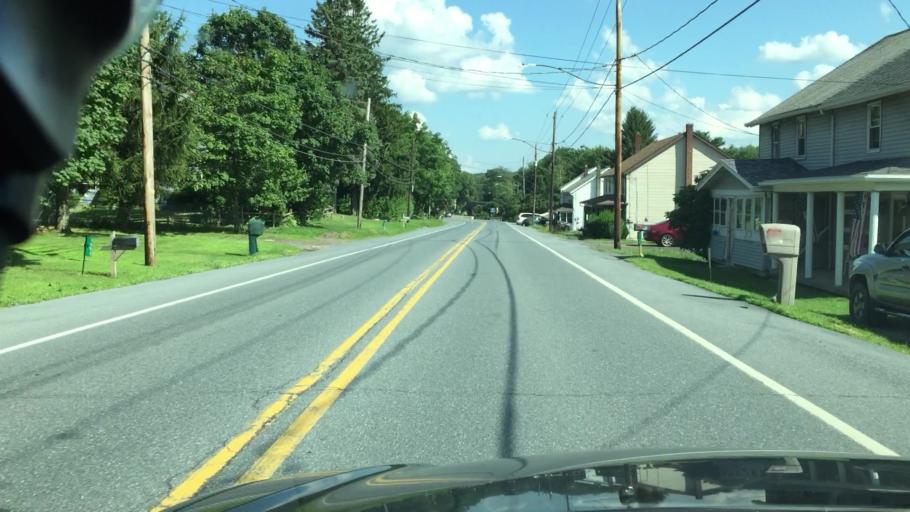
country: US
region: Pennsylvania
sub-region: Luzerne County
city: Hazleton
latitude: 40.9339
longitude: -75.9250
